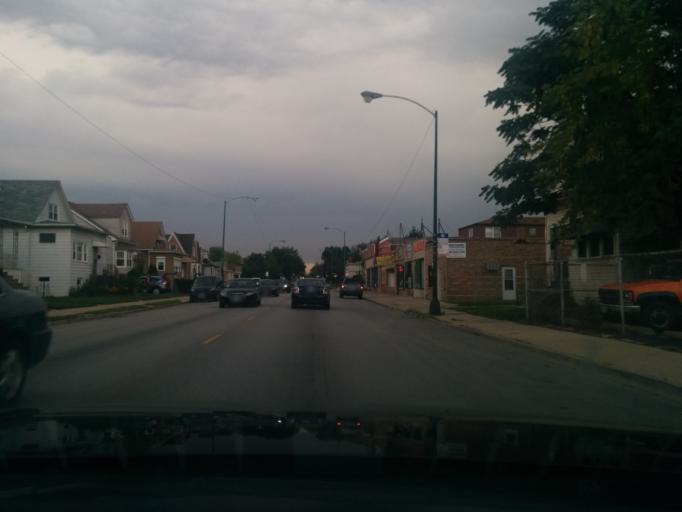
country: US
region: Illinois
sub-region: Cook County
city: Harwood Heights
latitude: 41.9458
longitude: -87.7815
